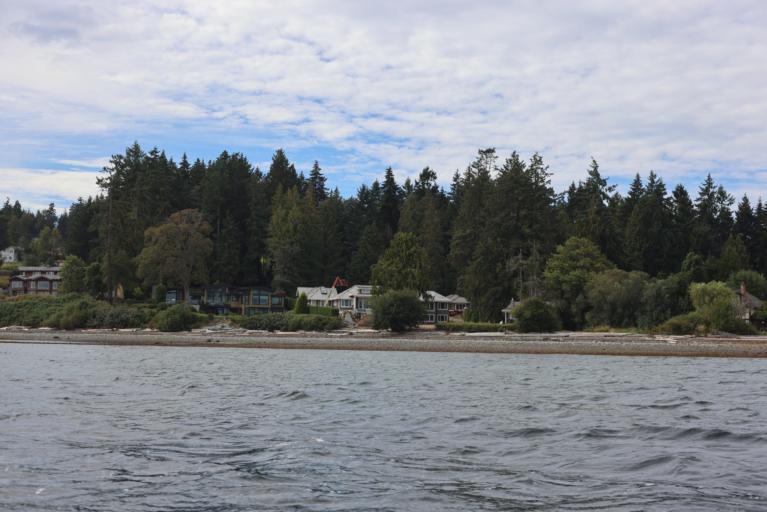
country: CA
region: British Columbia
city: Nanaimo
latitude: 49.2528
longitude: -124.0601
